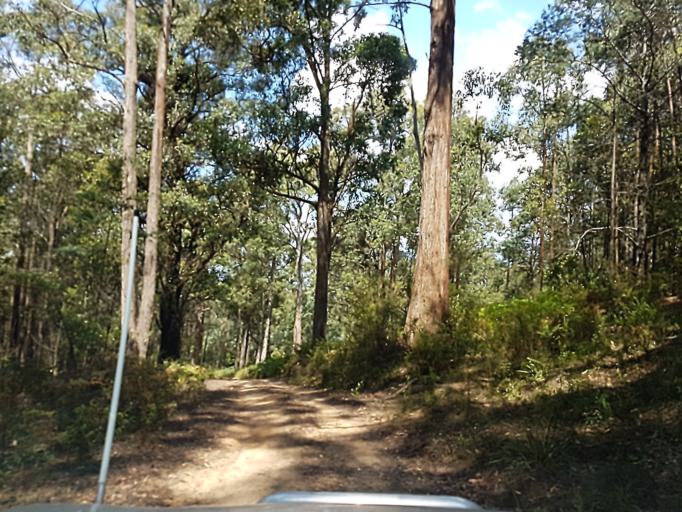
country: AU
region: Victoria
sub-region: East Gippsland
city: Lakes Entrance
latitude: -37.3915
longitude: 148.2925
